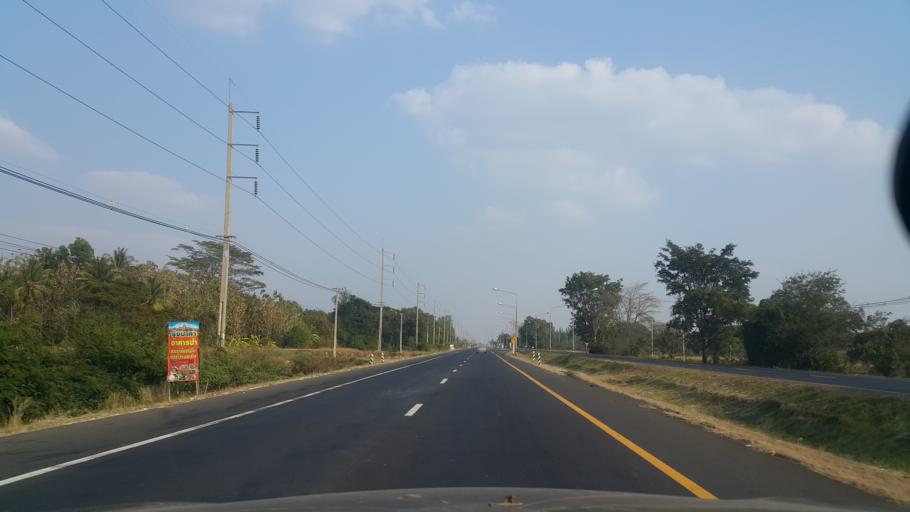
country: TH
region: Buriram
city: Chaloem Phra Kiat
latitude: 14.6189
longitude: 102.8953
